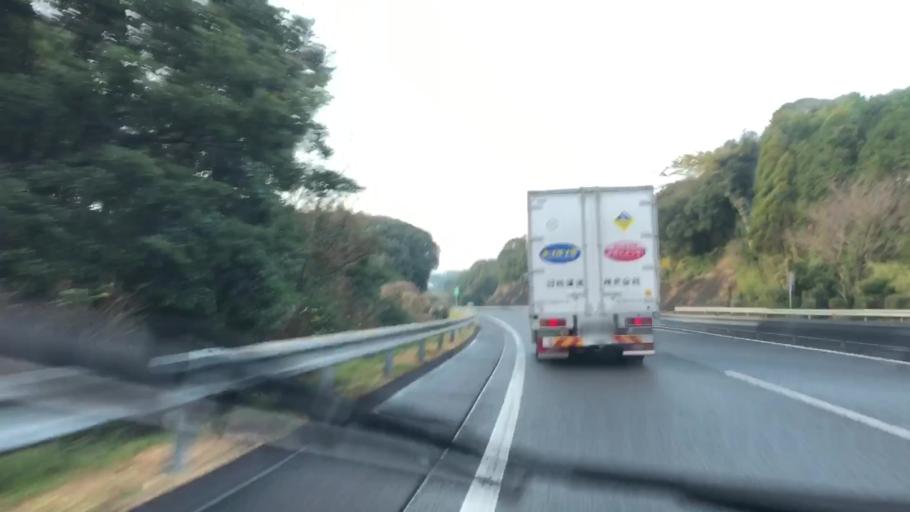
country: JP
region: Nagasaki
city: Sasebo
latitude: 33.1579
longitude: 129.8141
